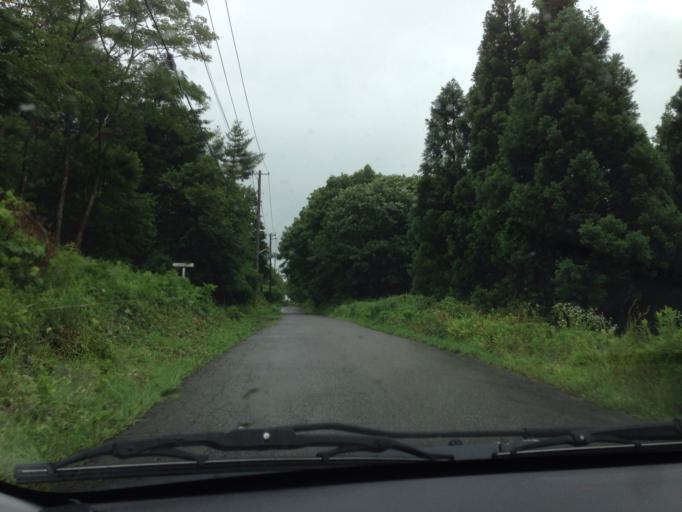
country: JP
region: Fukushima
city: Inawashiro
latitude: 37.5641
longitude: 140.0387
